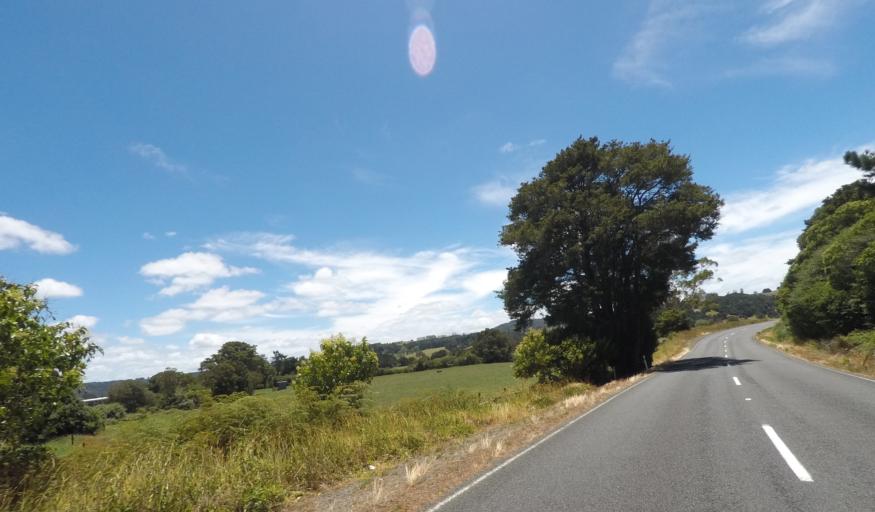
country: NZ
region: Northland
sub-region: Whangarei
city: Whangarei
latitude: -35.5380
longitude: 174.3100
